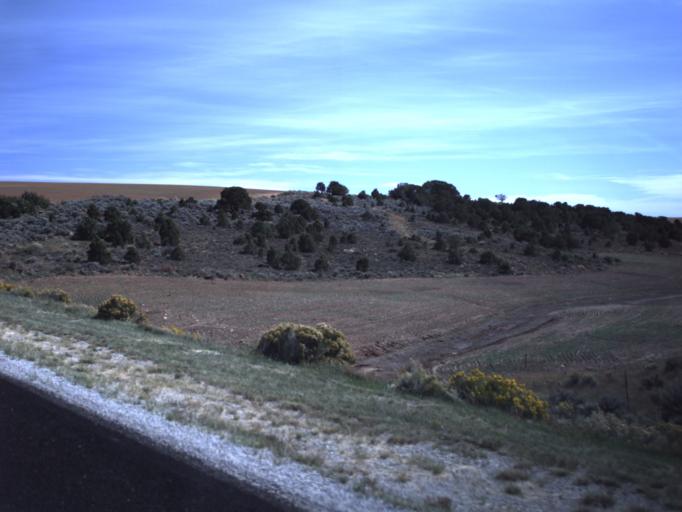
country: US
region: Utah
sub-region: San Juan County
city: Monticello
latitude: 37.8637
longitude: -109.2237
